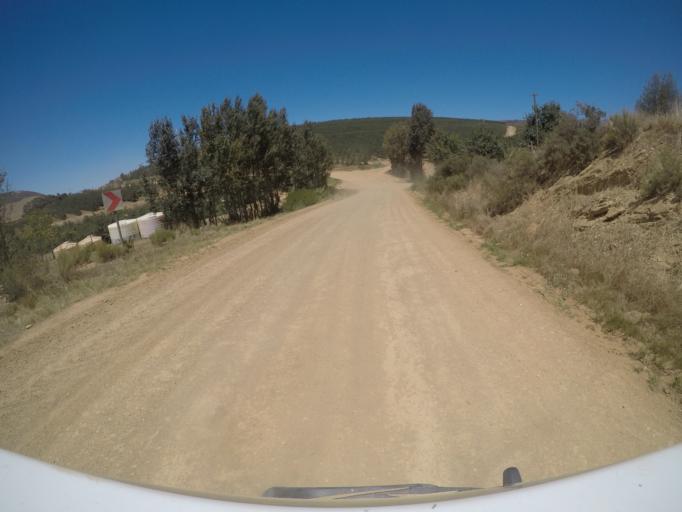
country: ZA
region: Western Cape
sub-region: Overberg District Municipality
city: Grabouw
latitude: -34.1024
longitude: 19.2065
